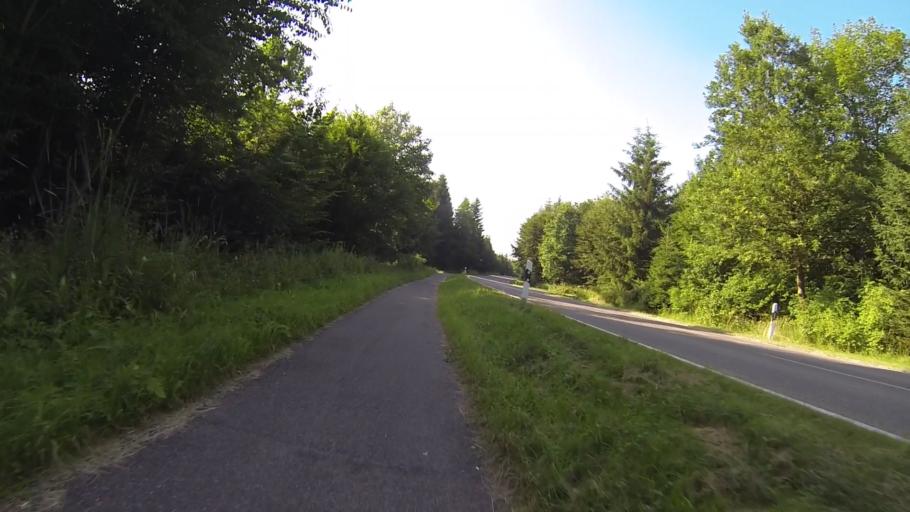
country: DE
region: Baden-Wuerttemberg
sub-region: Tuebingen Region
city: Staig
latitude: 48.3148
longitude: 9.9679
